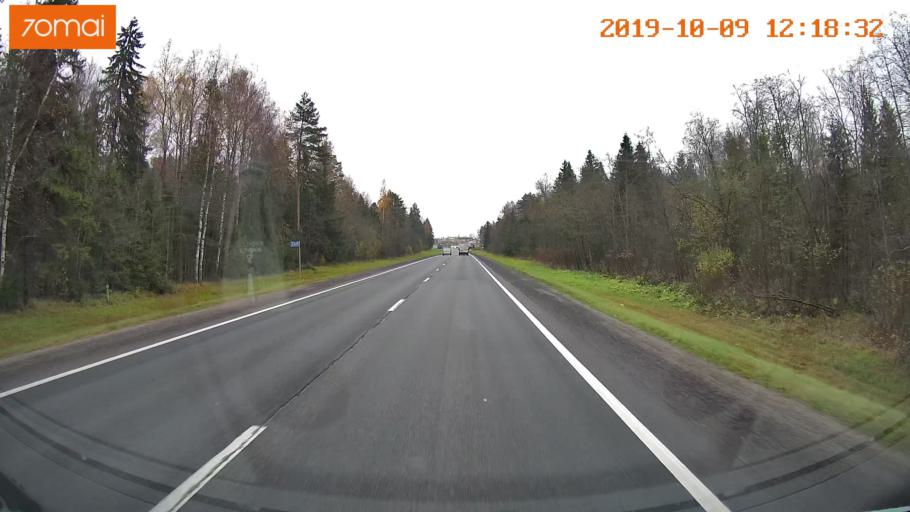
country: RU
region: Jaroslavl
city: Prechistoye
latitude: 58.4409
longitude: 40.3213
